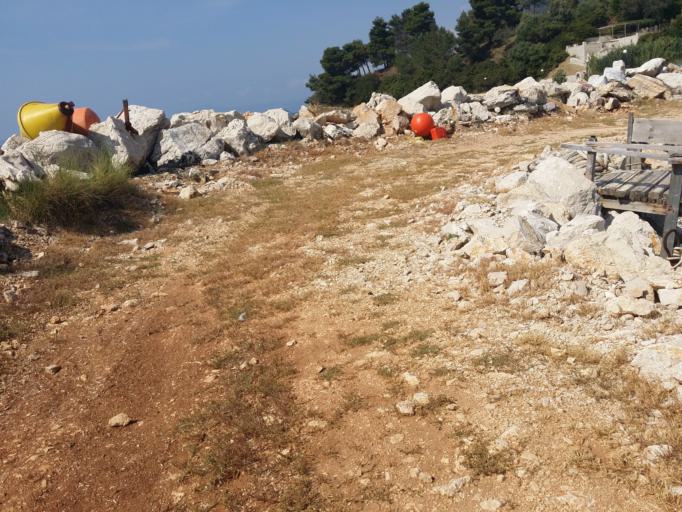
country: GR
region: West Greece
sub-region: Nomos Aitolias kai Akarnanias
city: Palairos
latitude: 38.7924
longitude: 20.8458
